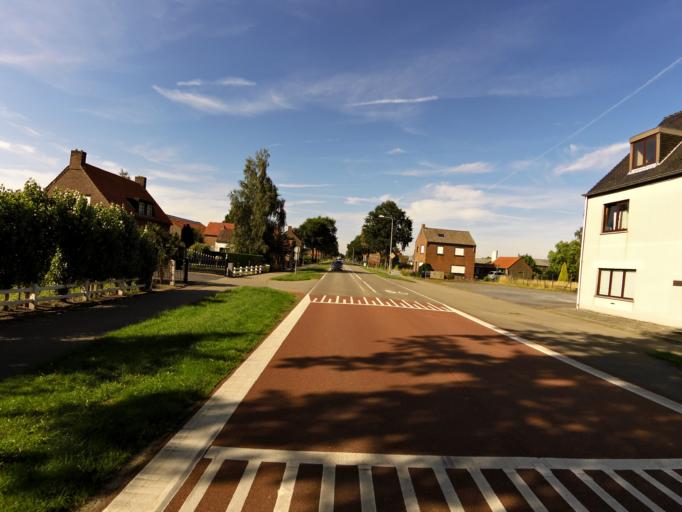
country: BE
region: Flanders
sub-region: Provincie Oost-Vlaanderen
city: Maldegem
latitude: 51.2417
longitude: 3.4484
